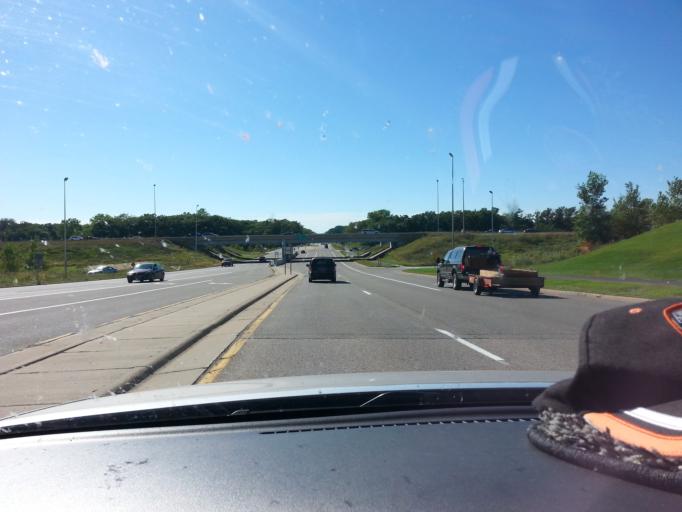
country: US
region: Minnesota
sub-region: Dakota County
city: Lakeville
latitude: 44.6815
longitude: -93.2912
